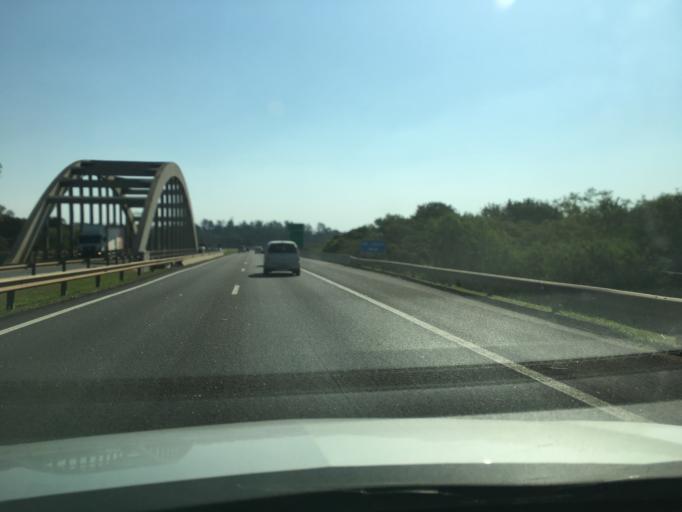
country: BR
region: Sao Paulo
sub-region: Sao Joao Da Boa Vista
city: Sao Joao da Boa Vista
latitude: -21.9922
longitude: -46.7972
